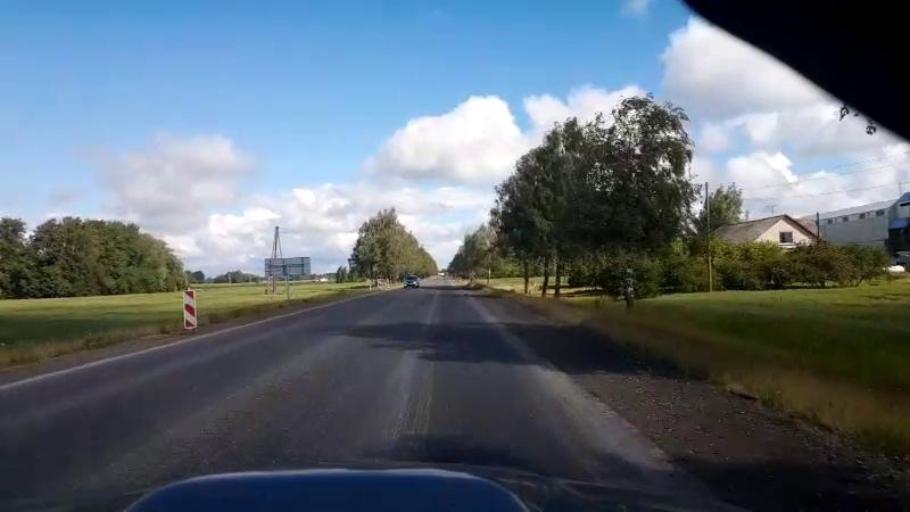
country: LV
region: Bauskas Rajons
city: Bauska
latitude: 56.3527
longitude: 24.2866
